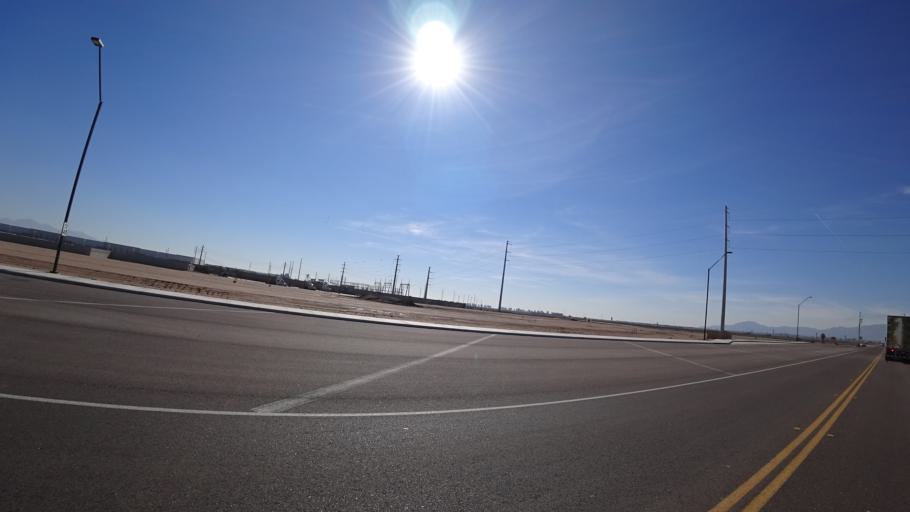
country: US
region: Arizona
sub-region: Maricopa County
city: Citrus Park
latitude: 33.5082
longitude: -112.4251
